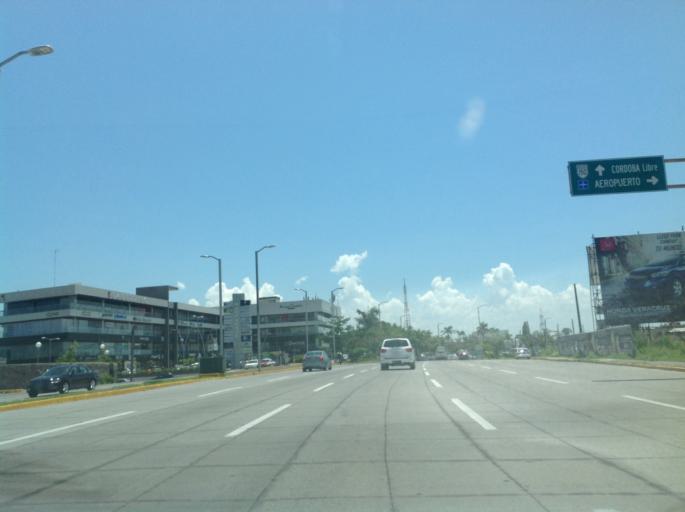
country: MX
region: Veracruz
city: Boca del Rio
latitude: 19.1368
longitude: -96.1040
